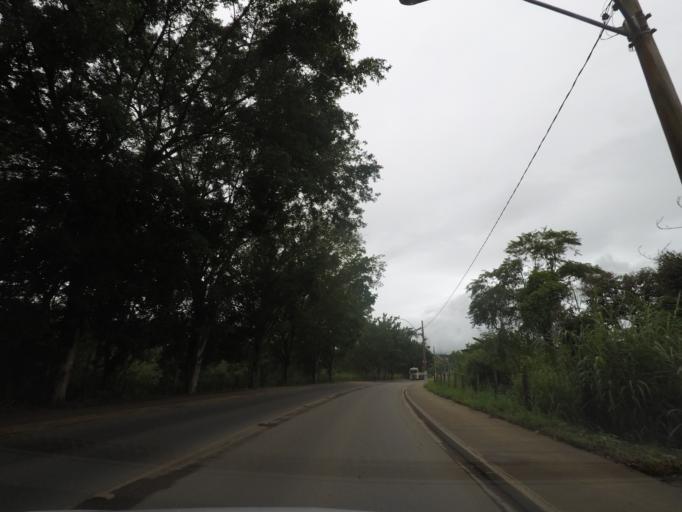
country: BR
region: Sao Paulo
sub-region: Cajati
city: Cajati
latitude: -24.7256
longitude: -48.0983
